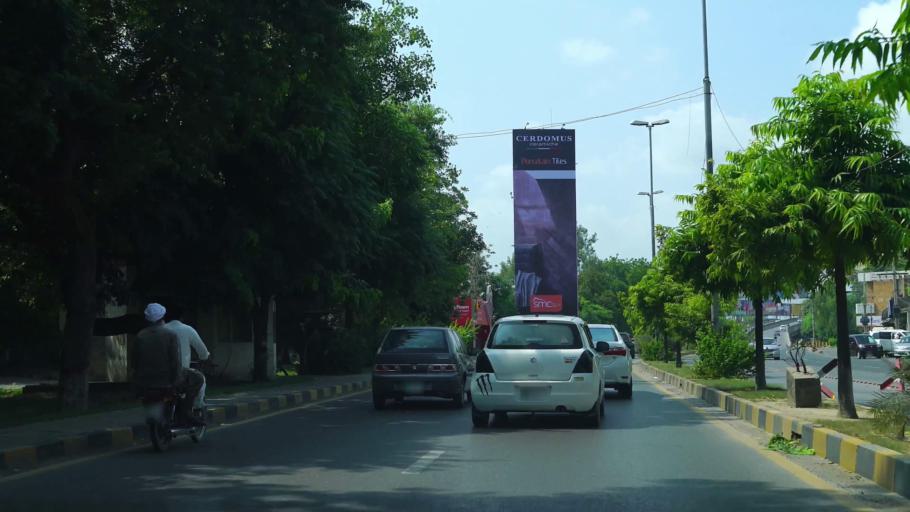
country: PK
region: Punjab
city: Lahore
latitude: 31.5267
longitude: 74.3627
